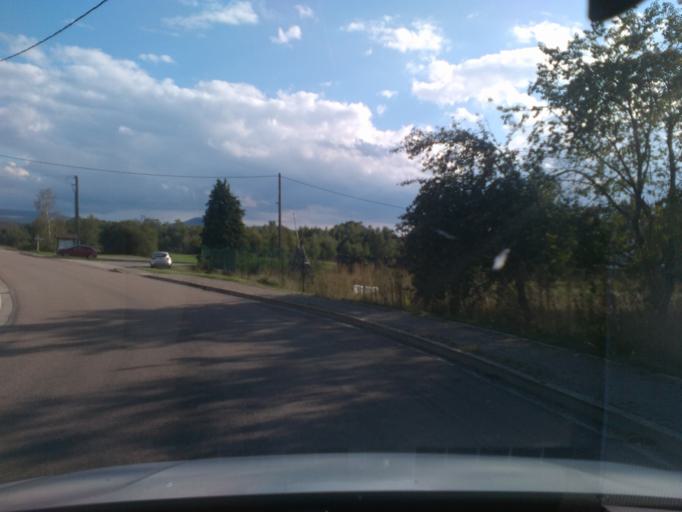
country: FR
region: Lorraine
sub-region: Departement des Vosges
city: Corcieux
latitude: 48.1979
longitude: 6.8781
